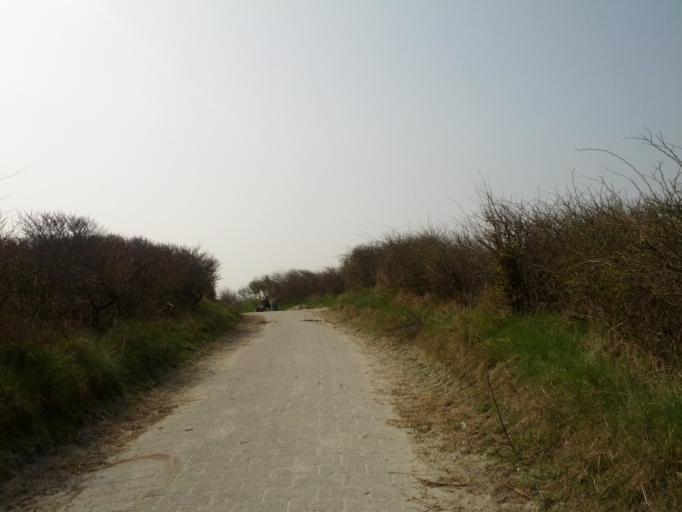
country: DE
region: Lower Saxony
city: Langeoog
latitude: 53.7551
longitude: 7.5188
